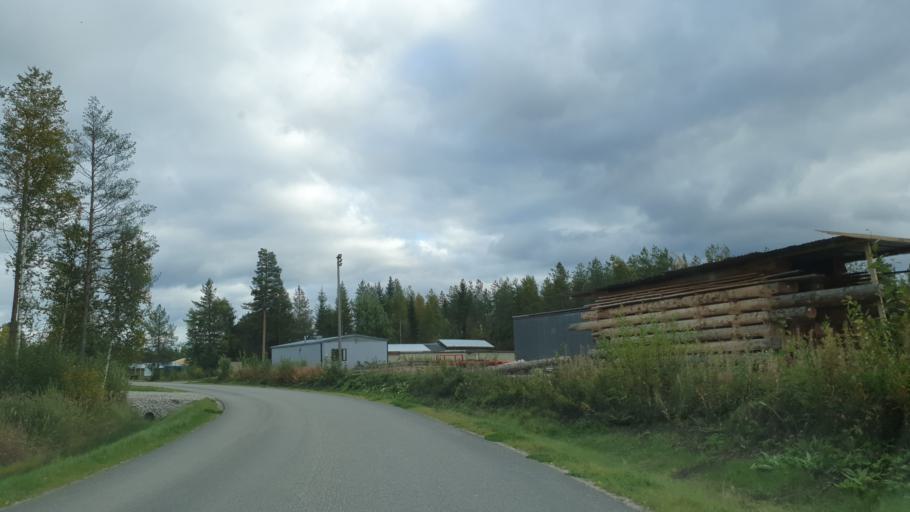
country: FI
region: Kainuu
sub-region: Kehys-Kainuu
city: Kuhmo
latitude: 64.1098
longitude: 29.4906
